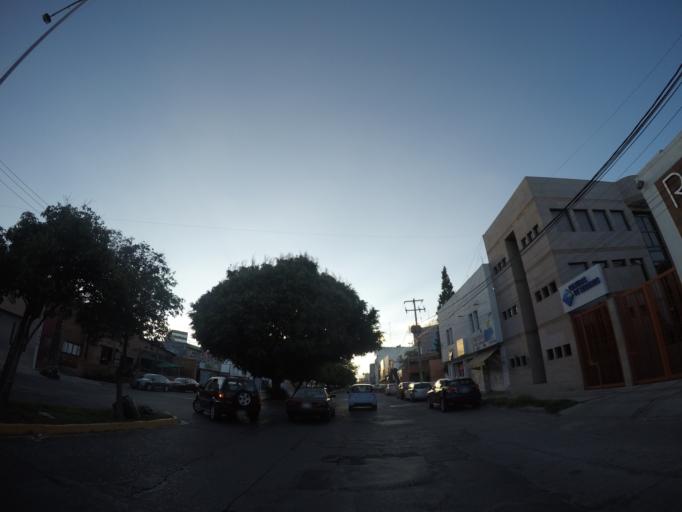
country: MX
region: San Luis Potosi
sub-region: San Luis Potosi
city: San Luis Potosi
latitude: 22.1415
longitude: -100.9963
